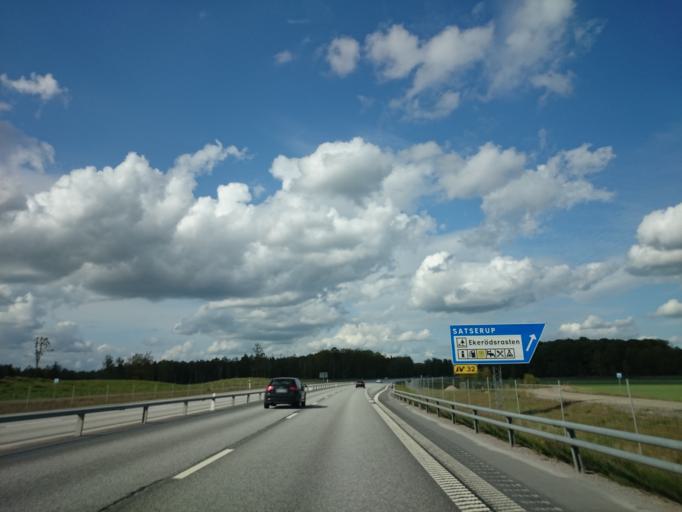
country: SE
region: Skane
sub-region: Horby Kommun
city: Hoerby
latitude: 55.8964
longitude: 13.7236
